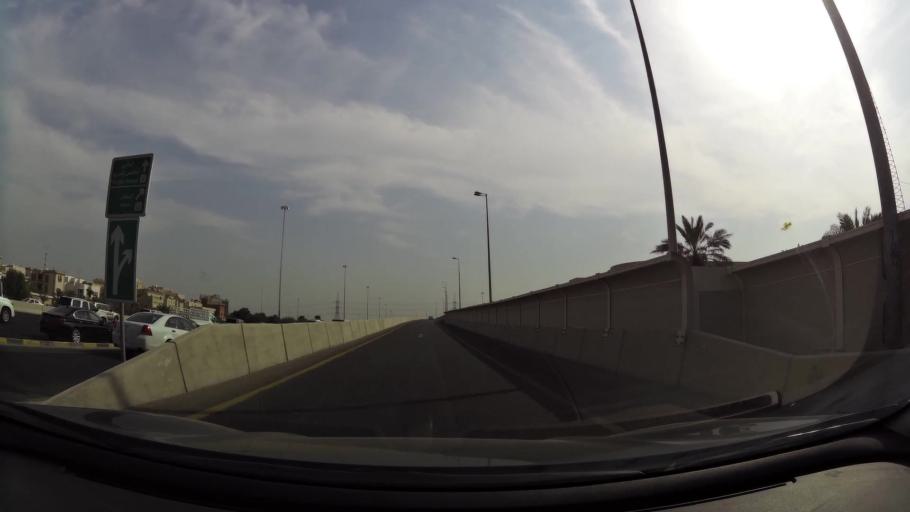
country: KW
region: Al Farwaniyah
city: Al Farwaniyah
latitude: 29.3092
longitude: 47.9769
